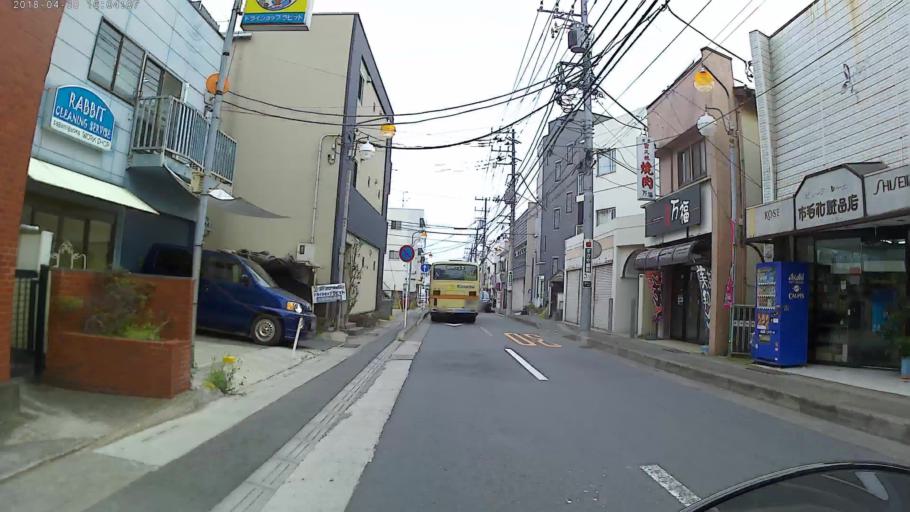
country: JP
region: Kanagawa
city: Minami-rinkan
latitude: 35.5109
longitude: 139.4233
